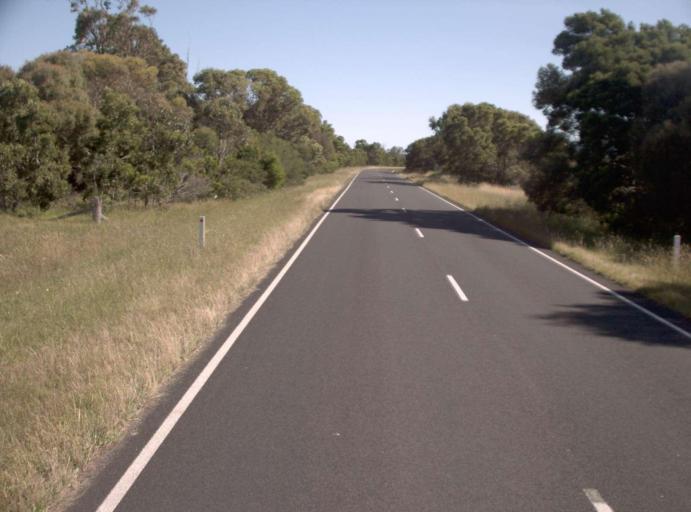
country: AU
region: Victoria
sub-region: Latrobe
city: Traralgon
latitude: -38.6311
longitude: 146.6762
